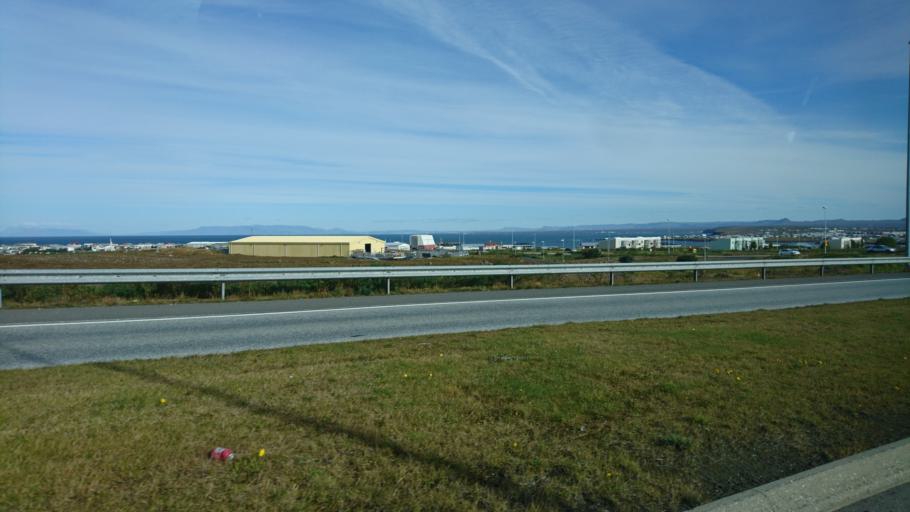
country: IS
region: Southern Peninsula
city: Reykjanesbaer
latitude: 63.9810
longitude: -22.5633
